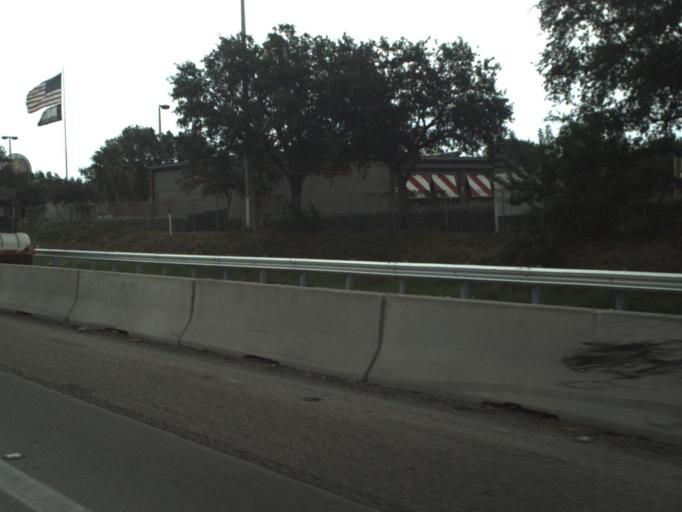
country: US
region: Florida
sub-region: Broward County
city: Dania Beach
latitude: 26.0382
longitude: -80.1634
